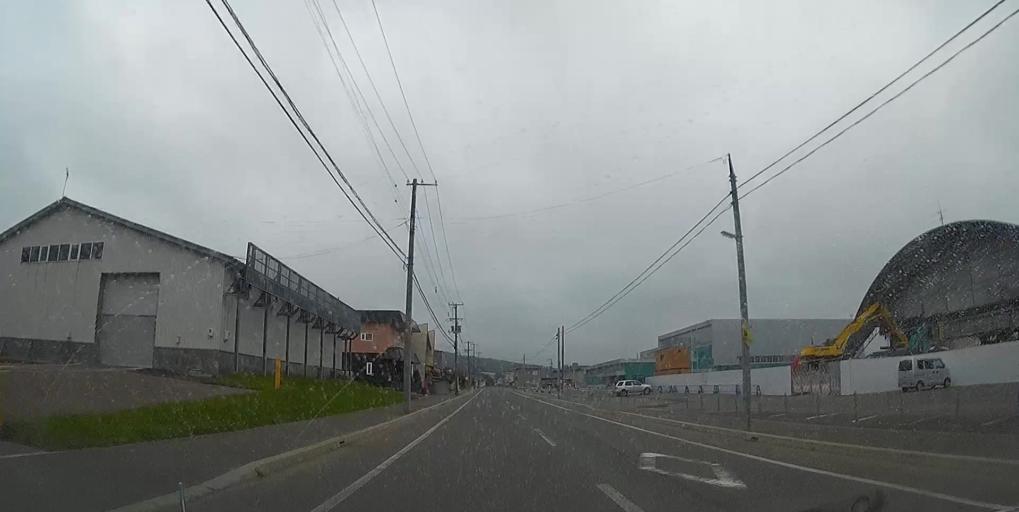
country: JP
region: Hokkaido
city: Iwanai
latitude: 42.4271
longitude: 140.0158
